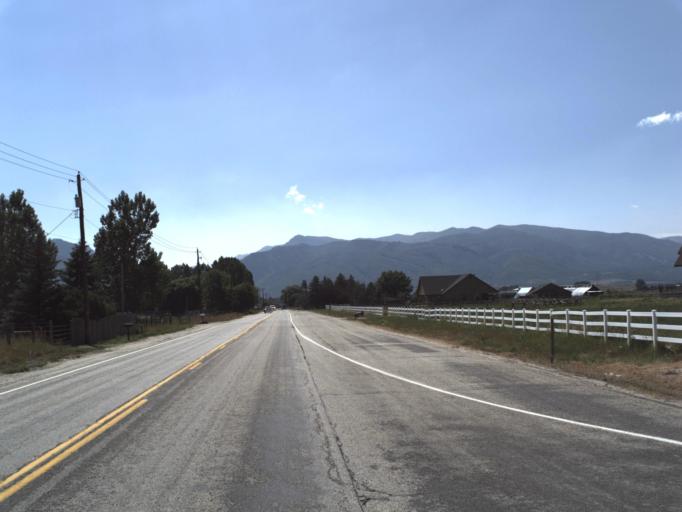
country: US
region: Utah
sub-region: Weber County
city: Wolf Creek
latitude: 41.2620
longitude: -111.7352
